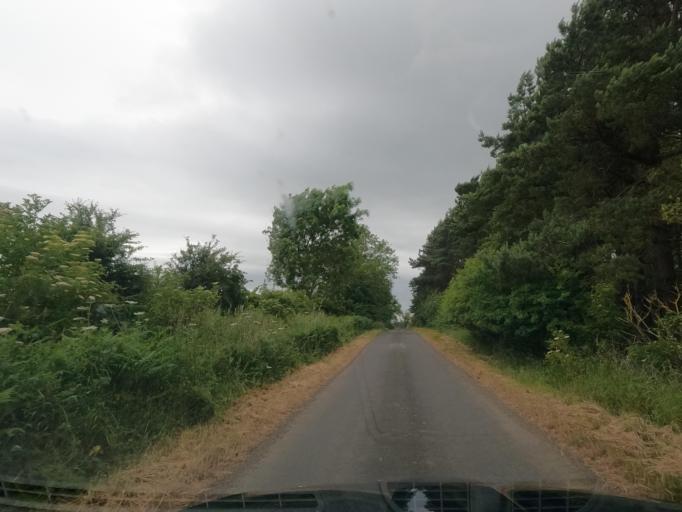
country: GB
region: England
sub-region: Northumberland
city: Ford
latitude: 55.6697
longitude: -2.0665
